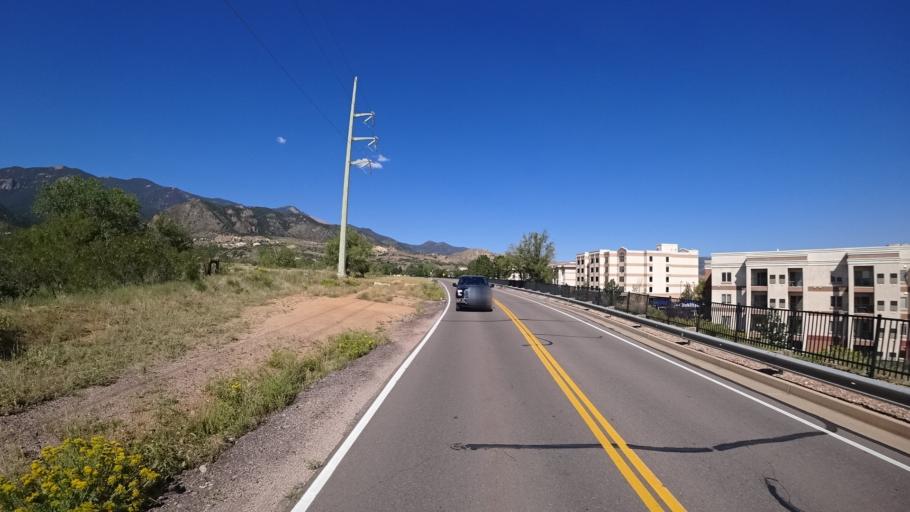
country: US
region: Colorado
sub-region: El Paso County
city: Colorado Springs
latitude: 38.8295
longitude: -104.8681
